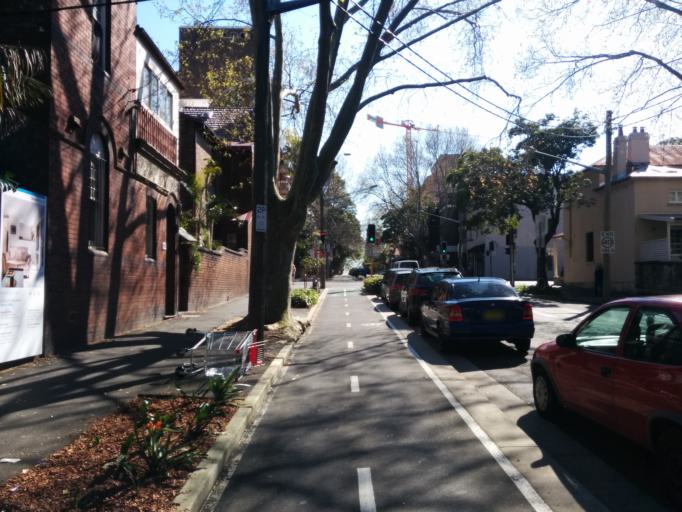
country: AU
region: New South Wales
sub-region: City of Sydney
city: Darlinghurst
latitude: -33.8844
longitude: 151.2159
